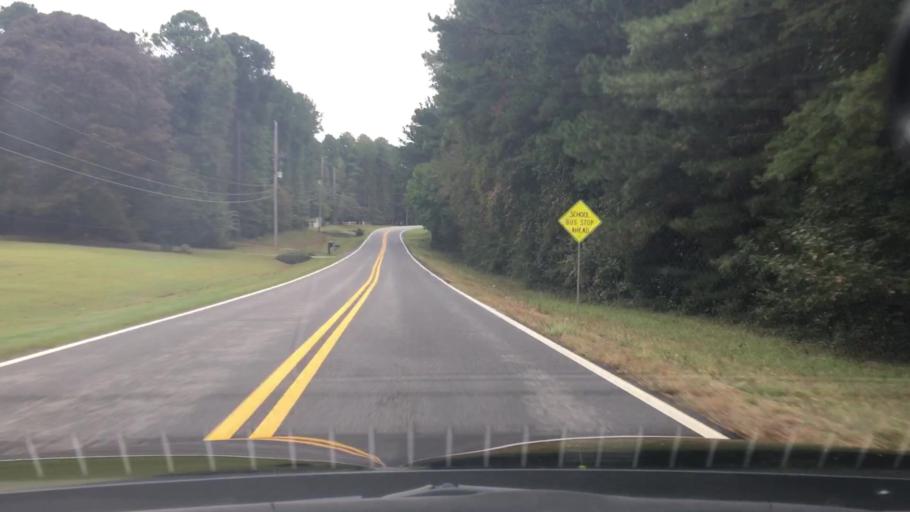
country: US
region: Georgia
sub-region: Coweta County
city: East Newnan
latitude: 33.4083
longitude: -84.7072
